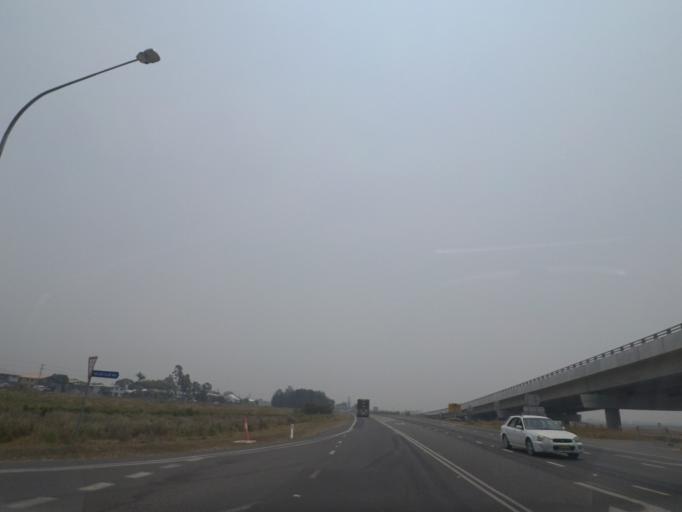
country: AU
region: New South Wales
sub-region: Clarence Valley
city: Maclean
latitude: -29.4249
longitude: 153.2412
